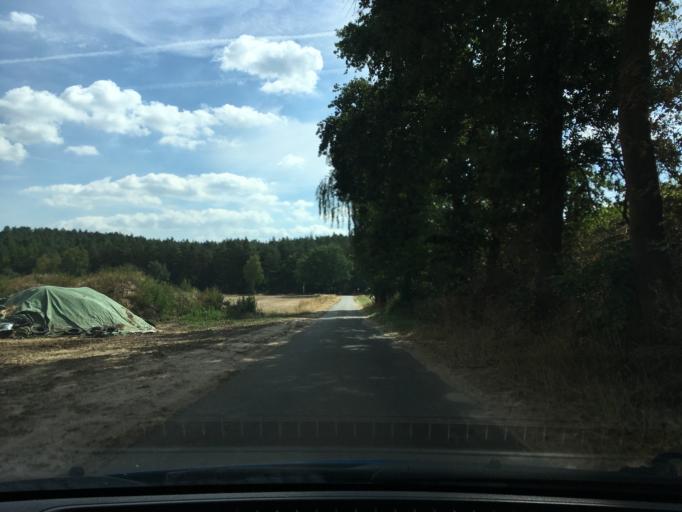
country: DE
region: Lower Saxony
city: Gohrde
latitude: 53.1213
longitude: 10.9496
